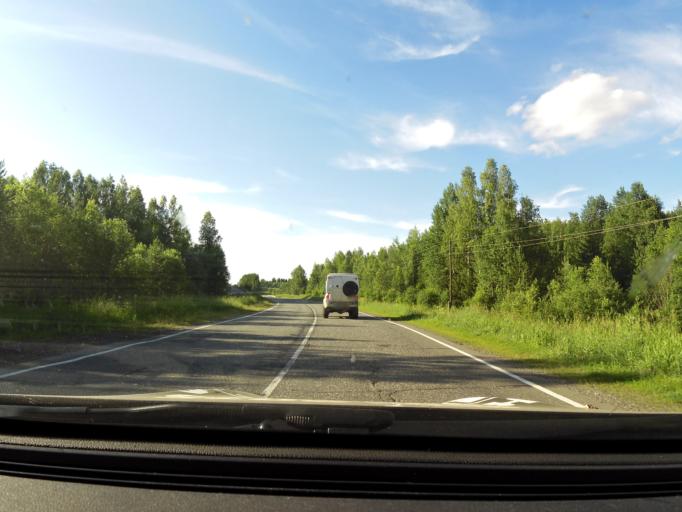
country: RU
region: Kirov
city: Belorechensk
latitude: 58.7411
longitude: 52.3458
